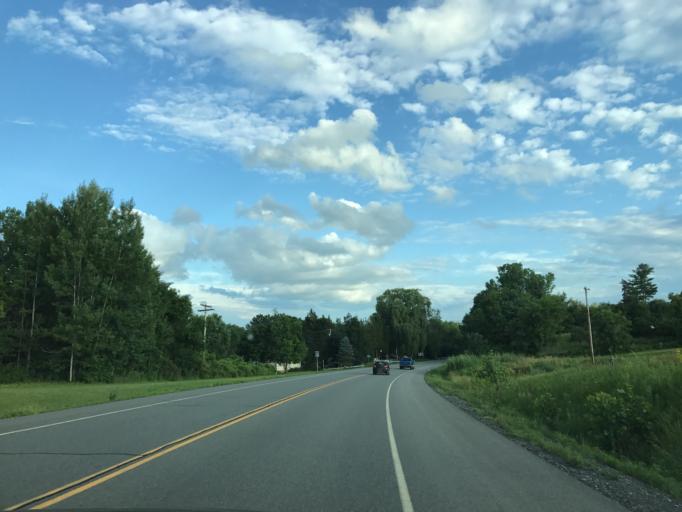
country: US
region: New York
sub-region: Saratoga County
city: Schuylerville
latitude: 43.0514
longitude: -73.5921
